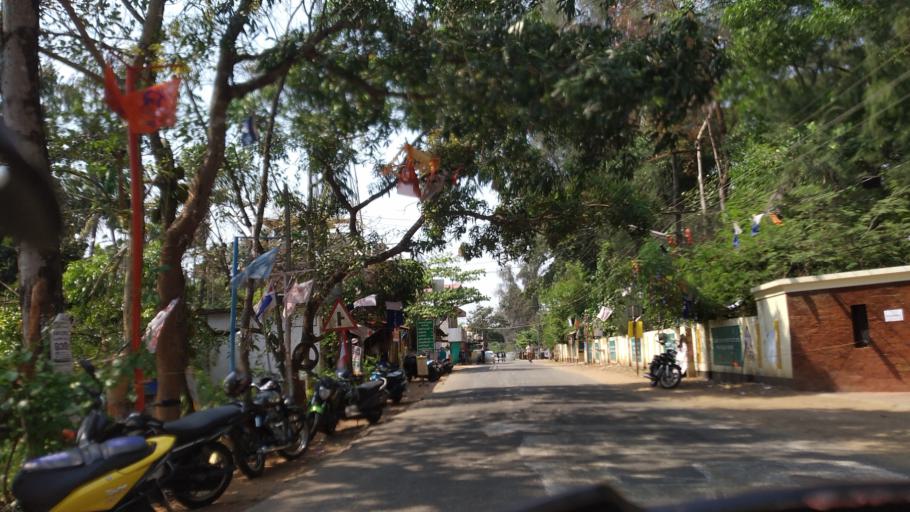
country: IN
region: Kerala
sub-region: Thrissur District
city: Kodungallur
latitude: 10.2666
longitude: 76.1423
